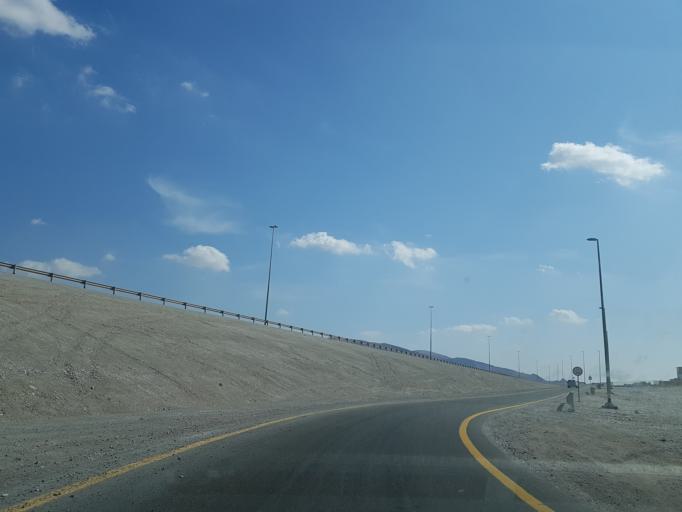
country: AE
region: Ra's al Khaymah
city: Ras al-Khaimah
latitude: 25.7984
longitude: 56.0300
